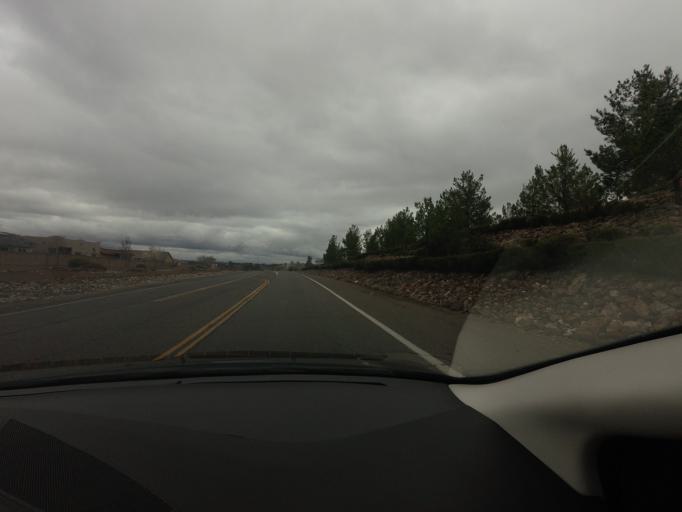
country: US
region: Arizona
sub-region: Yavapai County
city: Cottonwood
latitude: 34.7529
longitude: -112.0350
